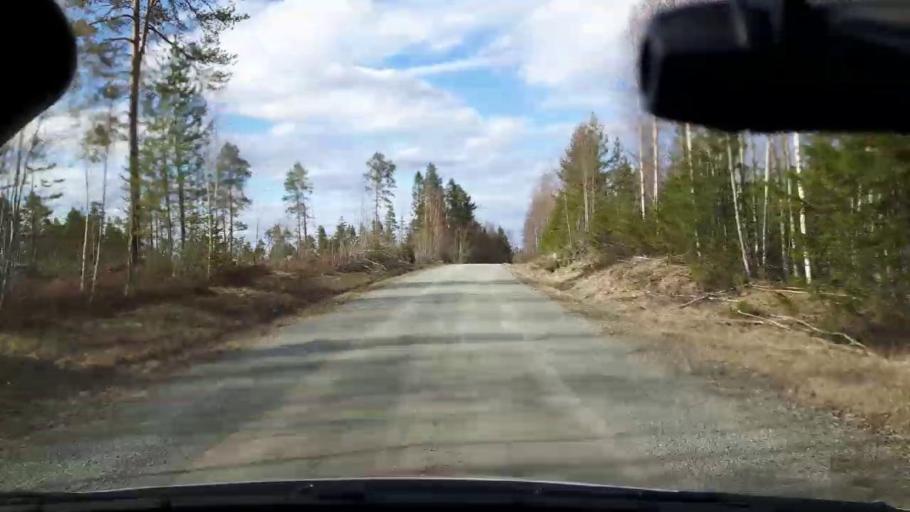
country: SE
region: Jaemtland
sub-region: Bergs Kommun
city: Hoverberg
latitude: 62.7524
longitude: 14.6624
